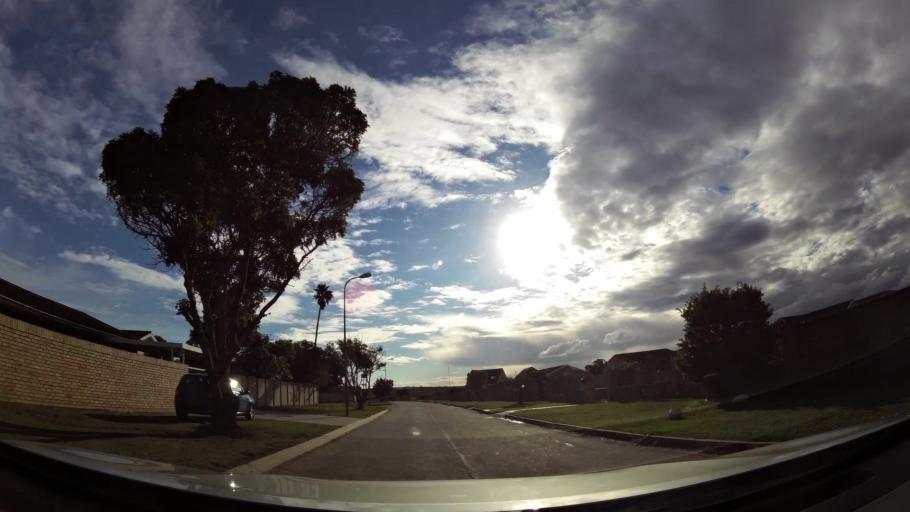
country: ZA
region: Eastern Cape
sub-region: Nelson Mandela Bay Metropolitan Municipality
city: Port Elizabeth
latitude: -33.9516
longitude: 25.4809
